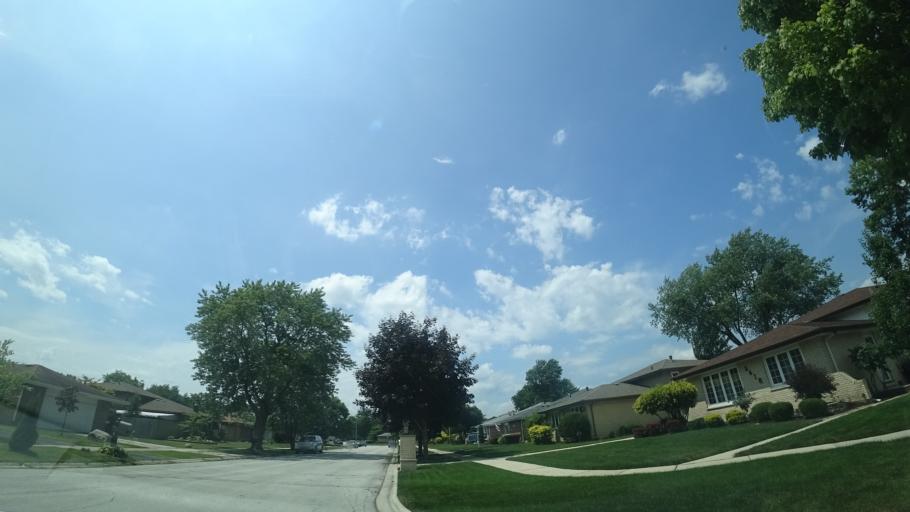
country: US
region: Illinois
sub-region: Cook County
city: Crestwood
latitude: 41.6585
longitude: -87.7554
